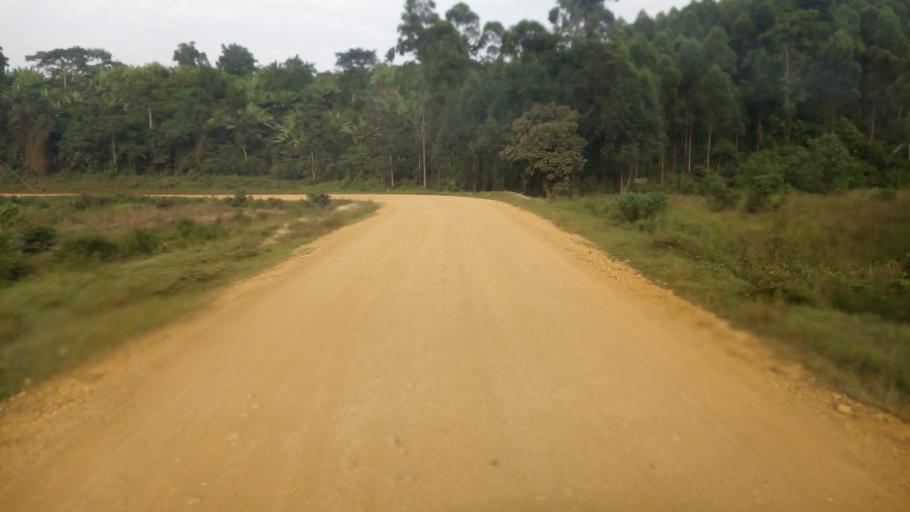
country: UG
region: Western Region
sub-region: Kanungu District
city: Ntungamo
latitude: -0.8392
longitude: 29.6407
